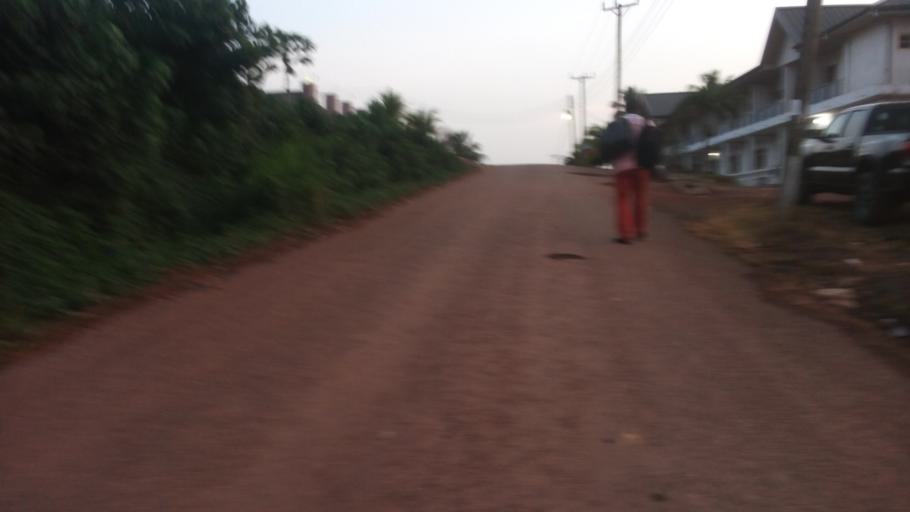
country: GH
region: Western
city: Tarkwa
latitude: 5.3065
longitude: -2.0011
